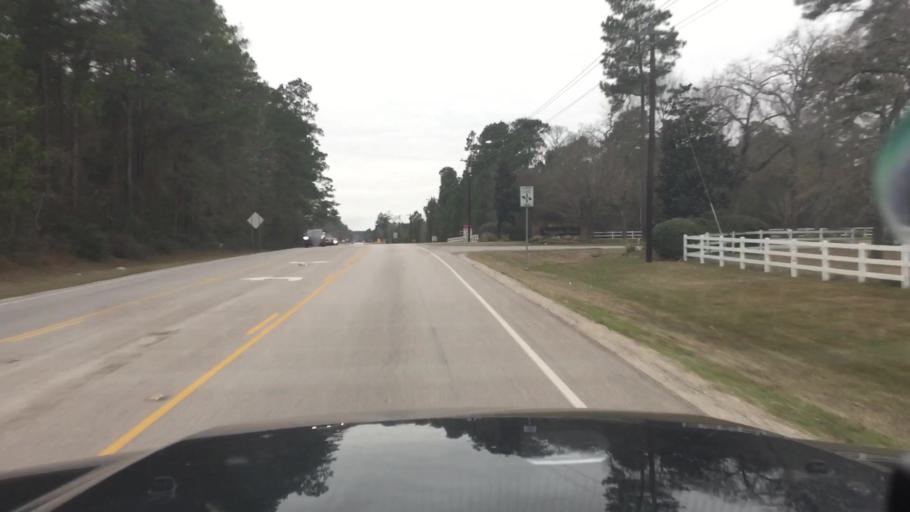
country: US
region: Texas
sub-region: Montgomery County
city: Magnolia
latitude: 30.1896
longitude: -95.8051
